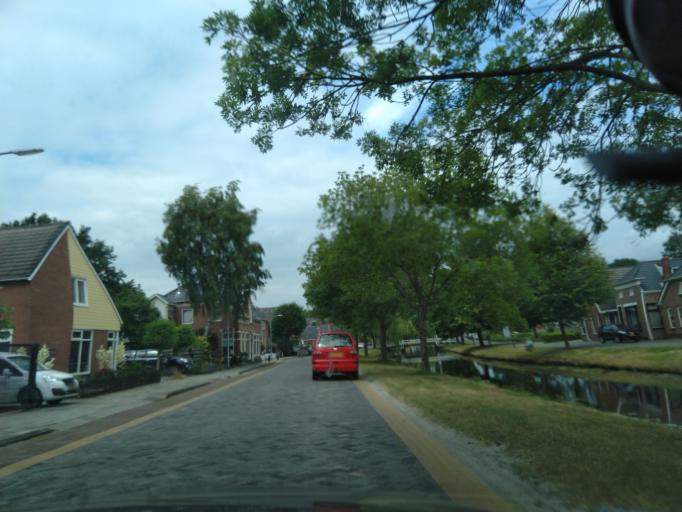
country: NL
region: Groningen
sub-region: Gemeente Pekela
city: Oude Pekela
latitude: 53.0971
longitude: 6.9927
